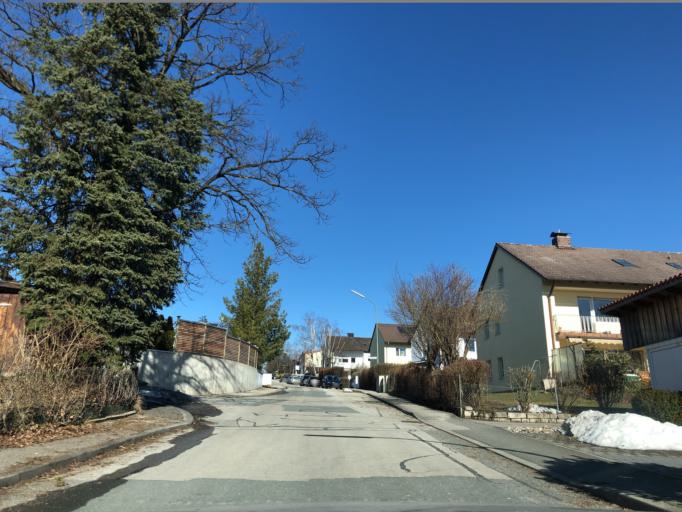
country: DE
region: Bavaria
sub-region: Upper Bavaria
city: Ebersberg
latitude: 48.0705
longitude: 11.9640
